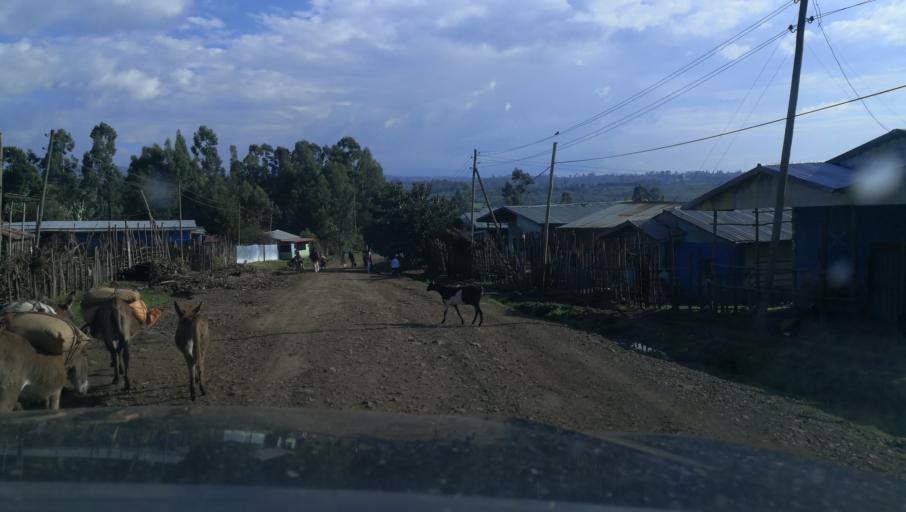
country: ET
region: Oromiya
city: Tulu Bolo
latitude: 8.4602
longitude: 38.2515
